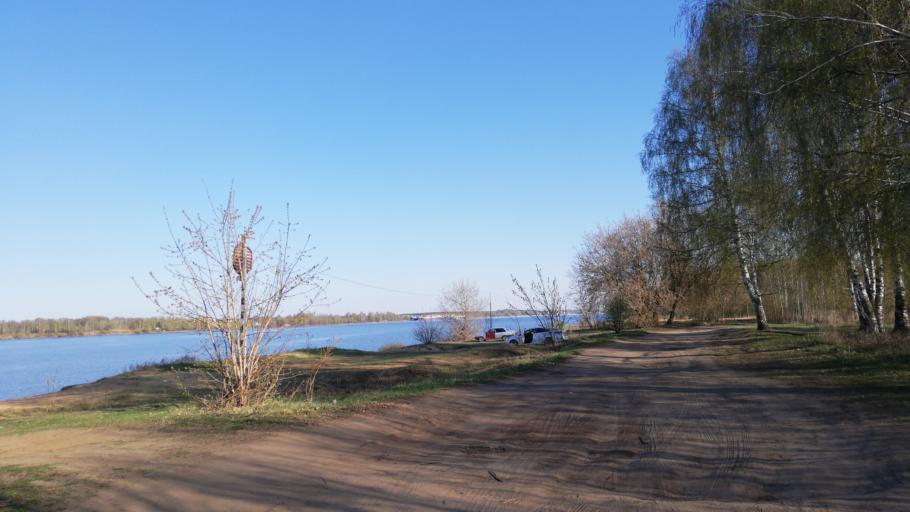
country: RU
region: Jaroslavl
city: Yaroslavl
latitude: 57.6137
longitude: 39.9061
